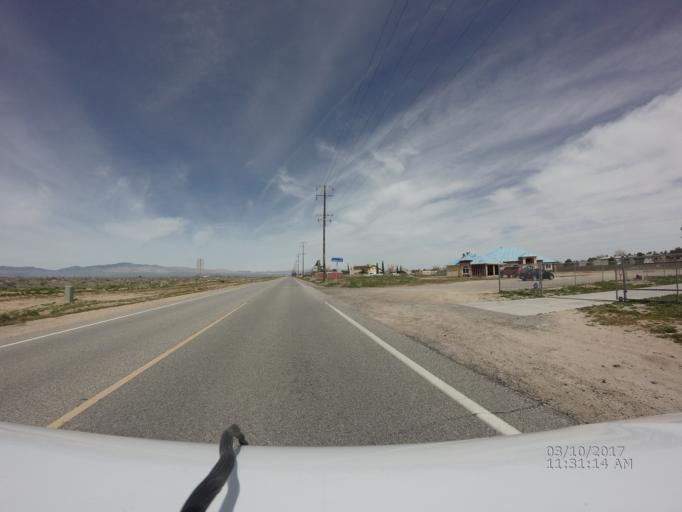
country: US
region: California
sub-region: Los Angeles County
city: Quartz Hill
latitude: 34.7636
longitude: -118.2900
